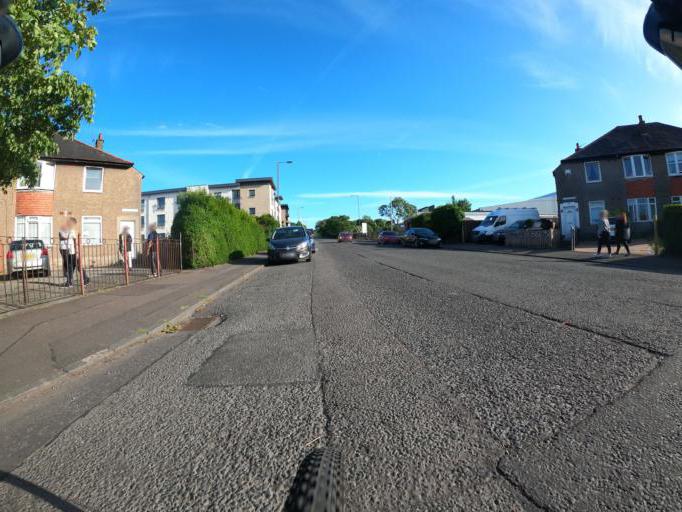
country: GB
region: Scotland
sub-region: Edinburgh
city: Edinburgh
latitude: 55.9724
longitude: -3.2303
